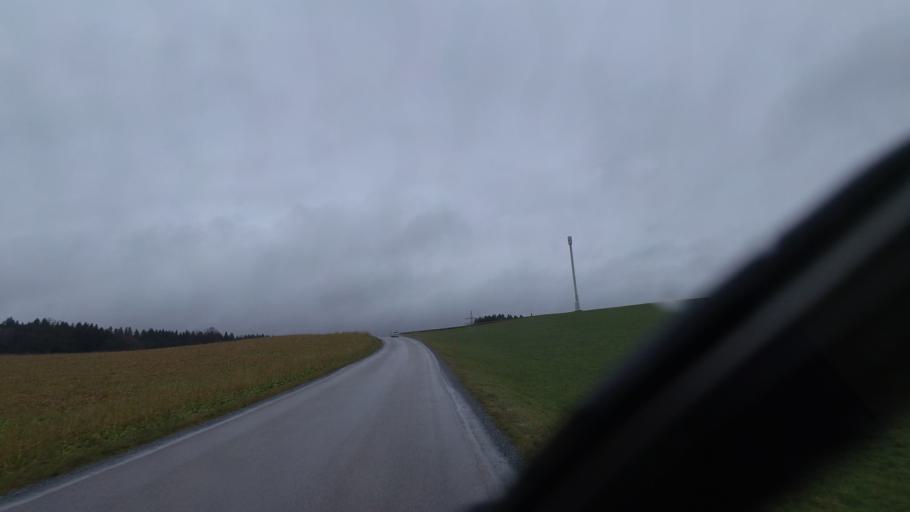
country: DE
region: Bavaria
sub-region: Upper Bavaria
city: Nussdorf
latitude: 47.9078
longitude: 12.6000
